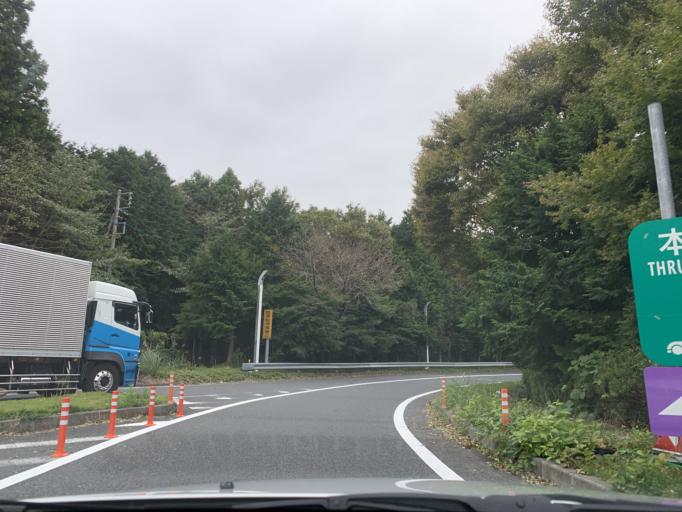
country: JP
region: Shizuoka
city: Gotemba
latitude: 35.3140
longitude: 138.9618
